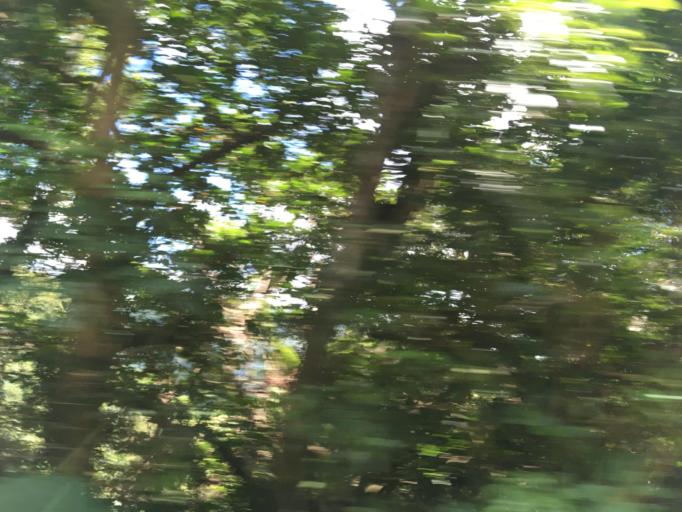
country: TW
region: Taipei
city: Taipei
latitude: 24.9363
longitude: 121.5815
